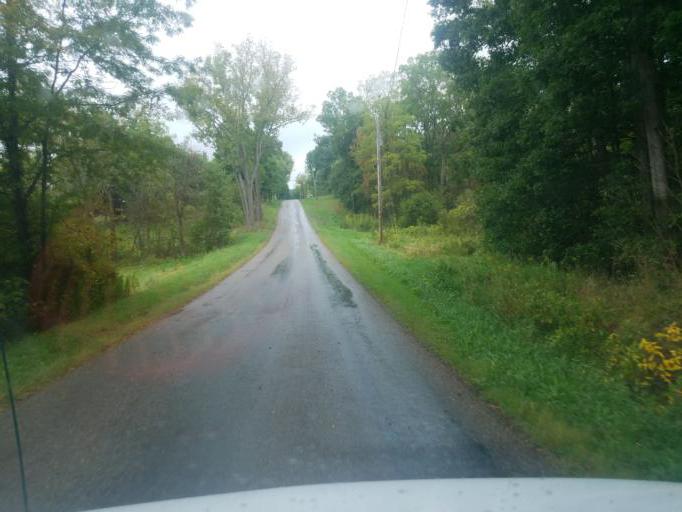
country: US
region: Ohio
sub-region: Wayne County
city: West Salem
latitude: 40.9352
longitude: -82.1233
